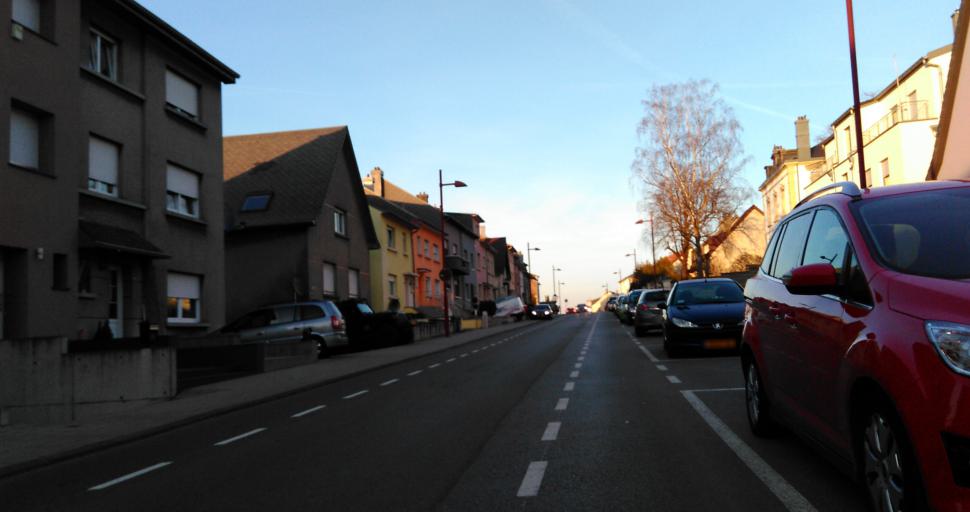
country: LU
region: Luxembourg
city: Lamadelaine
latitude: 49.5485
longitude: 5.8518
